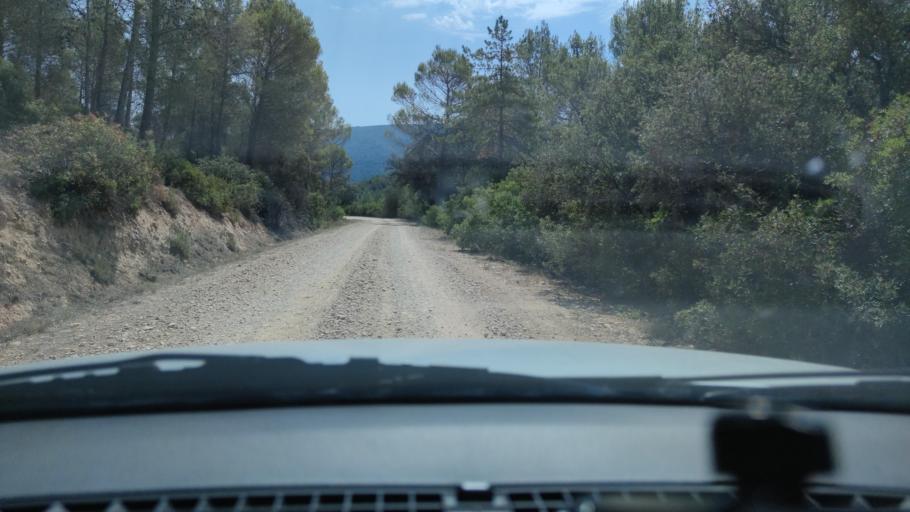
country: ES
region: Catalonia
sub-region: Provincia de Lleida
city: Camarasa
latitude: 41.9246
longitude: 0.8431
